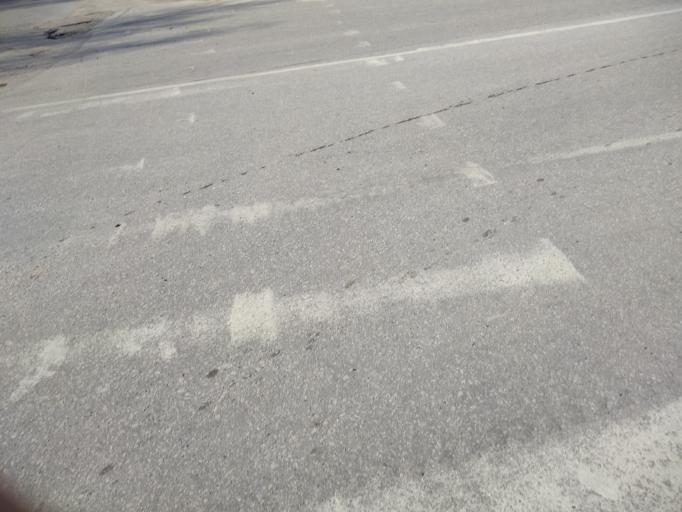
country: RU
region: Komi Republic
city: Pechora
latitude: 65.1236
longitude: 57.1543
